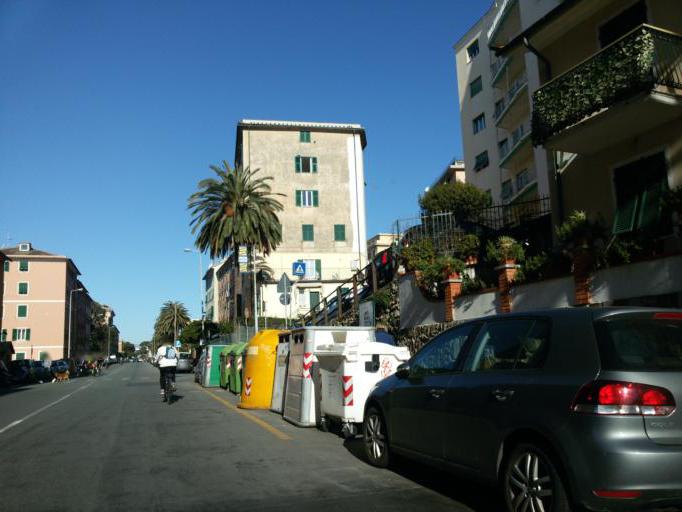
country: IT
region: Liguria
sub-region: Provincia di Genova
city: Bogliasco
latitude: 44.3832
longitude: 9.0248
